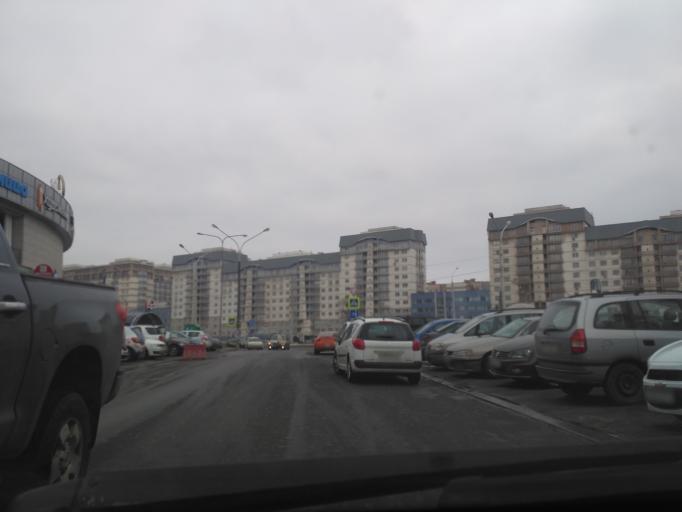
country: BY
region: Minsk
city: Borovlyany
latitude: 53.9461
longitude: 27.6870
